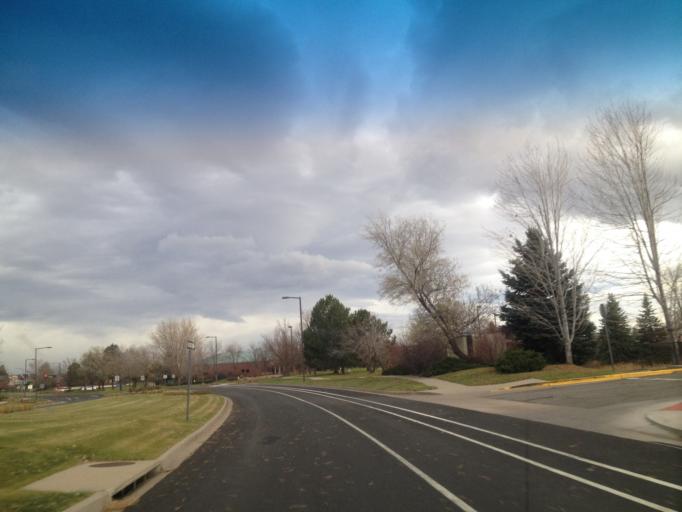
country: US
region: Colorado
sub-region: Boulder County
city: Superior
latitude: 39.9646
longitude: -105.1663
